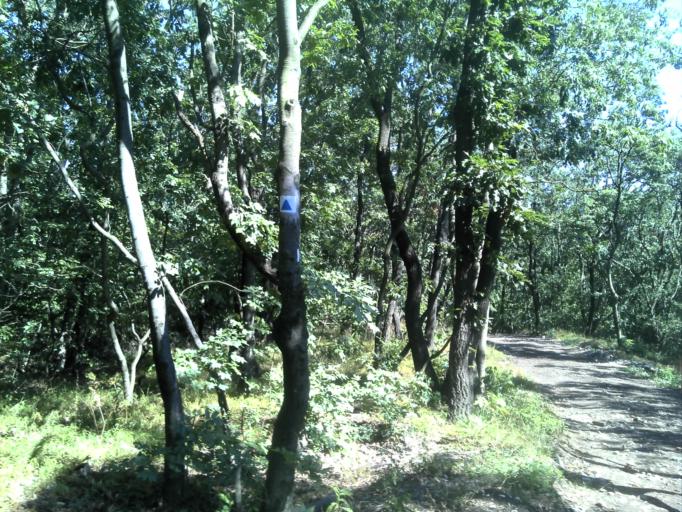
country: HU
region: Pest
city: Piliscsaba
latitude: 47.6474
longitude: 18.8371
